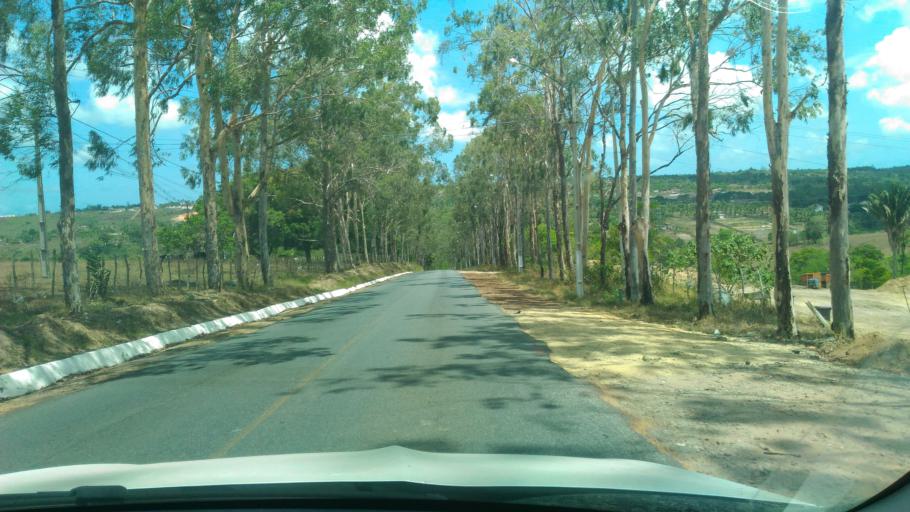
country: BR
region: Paraiba
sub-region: Conde
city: Conde
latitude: -7.2626
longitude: -34.9289
